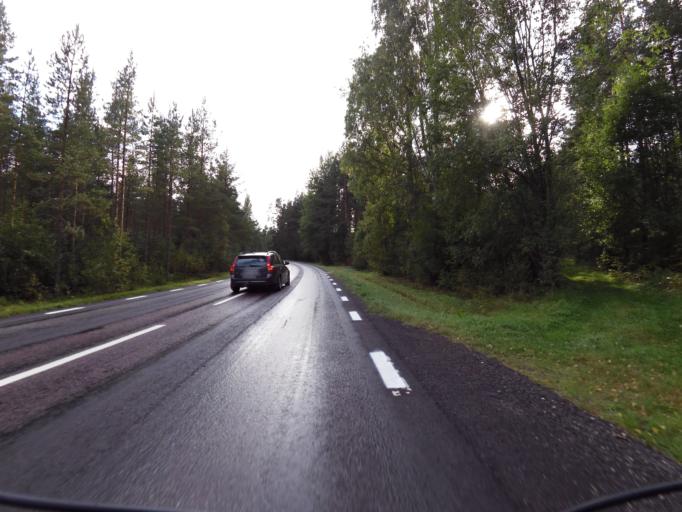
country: SE
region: Gaevleborg
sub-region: Ockelbo Kommun
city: Ockelbo
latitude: 60.8316
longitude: 16.6985
